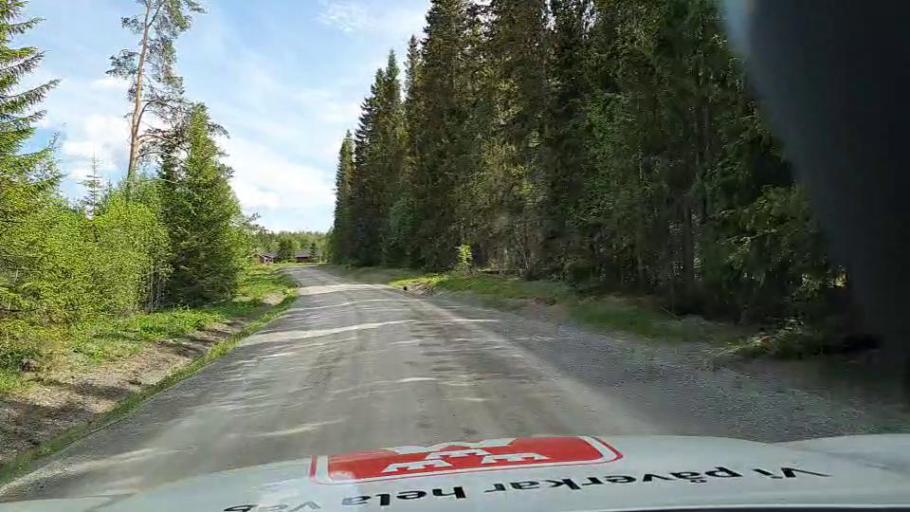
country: SE
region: Jaemtland
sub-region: OEstersunds Kommun
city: Brunflo
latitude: 63.0167
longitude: 14.7721
